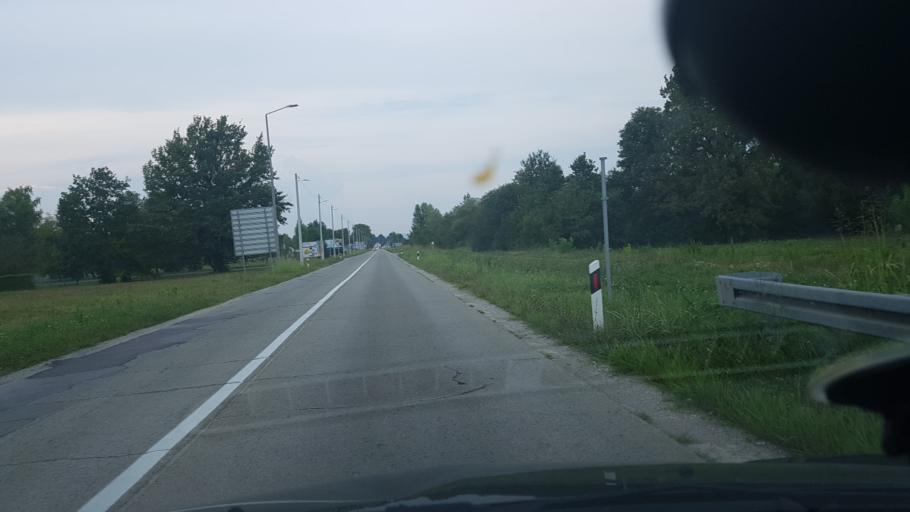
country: HR
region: Zagrebacka
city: Bregana
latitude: 45.8259
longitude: 15.7027
